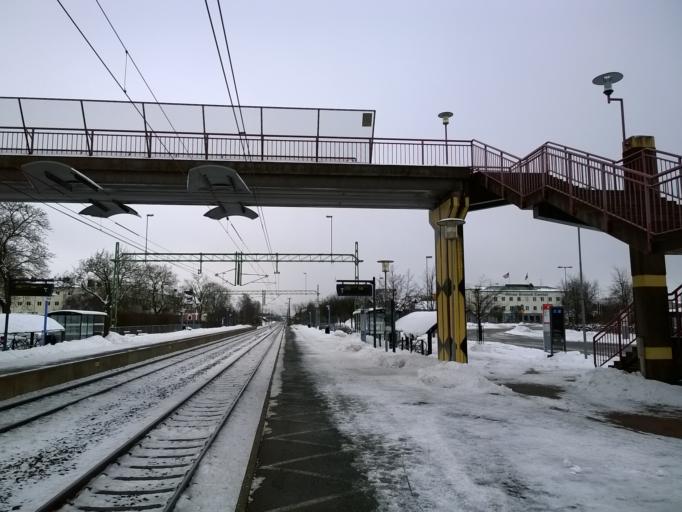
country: SE
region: Joenkoeping
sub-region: Savsjo Kommun
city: Saevsjoe
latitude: 57.4028
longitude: 14.6654
